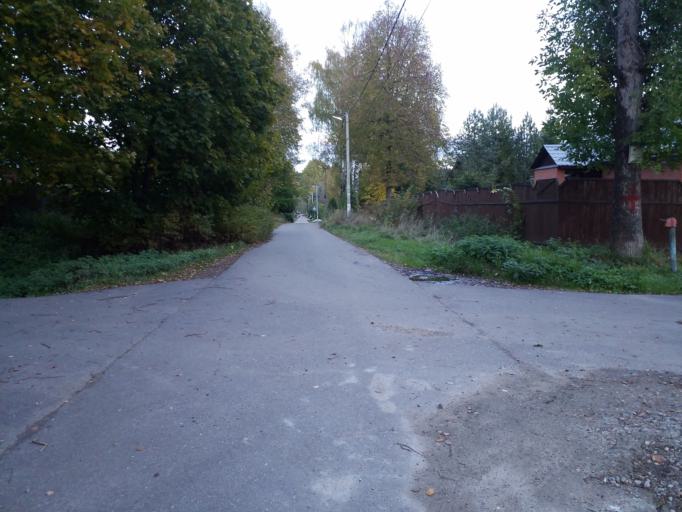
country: RU
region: Moskovskaya
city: Ashukino
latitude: 56.1680
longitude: 37.9579
